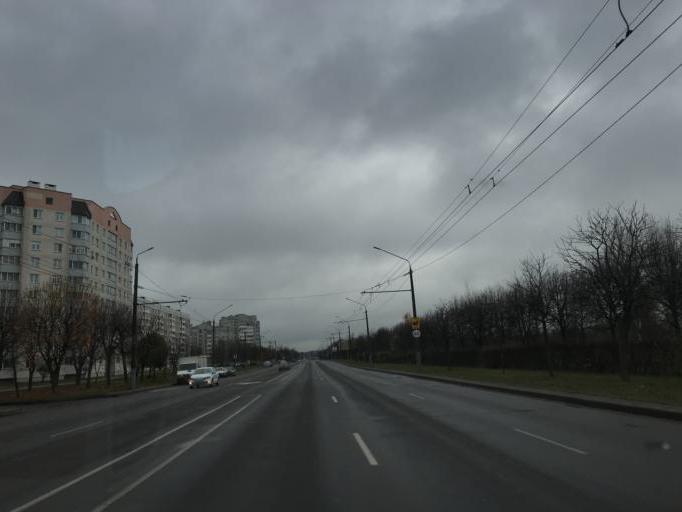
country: BY
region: Mogilev
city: Mahilyow
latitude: 53.8679
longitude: 30.3279
